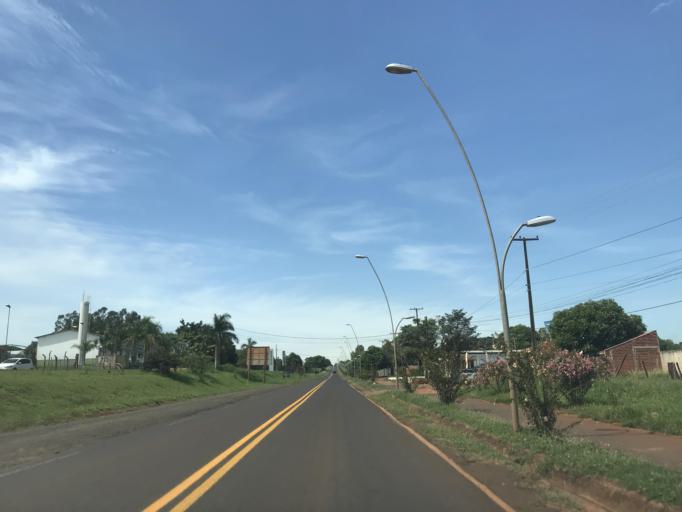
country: BR
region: Parana
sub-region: Terra Rica
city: Terra Rica
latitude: -22.7412
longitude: -52.6248
